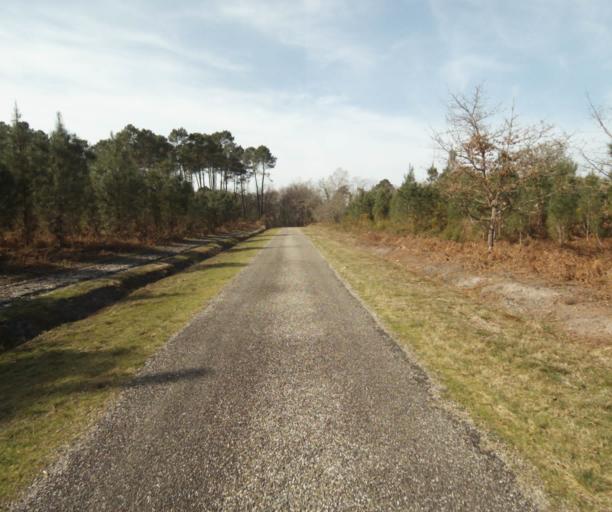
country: FR
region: Aquitaine
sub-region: Departement des Landes
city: Roquefort
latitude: 44.1352
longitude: -0.1959
